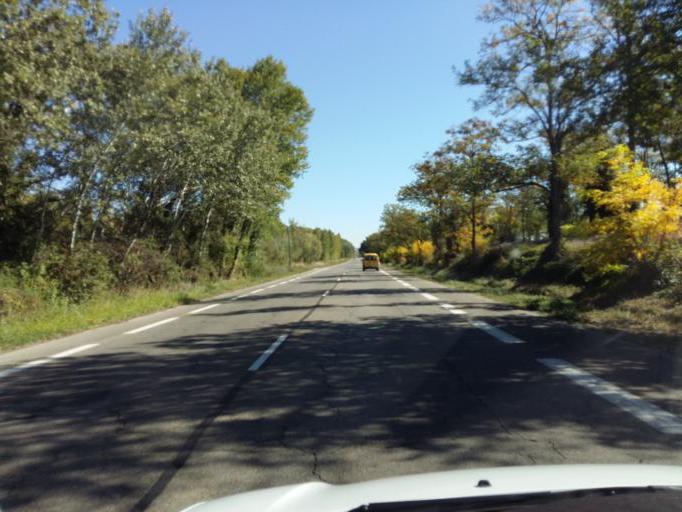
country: FR
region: Provence-Alpes-Cote d'Azur
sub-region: Departement des Bouches-du-Rhone
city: Charleval
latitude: 43.7502
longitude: 5.2728
